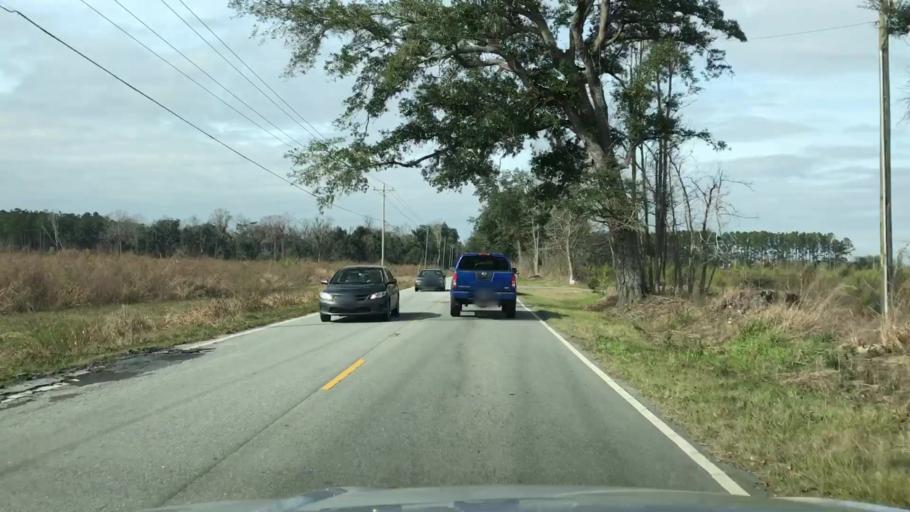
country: US
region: South Carolina
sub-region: Charleston County
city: Shell Point
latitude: 32.7725
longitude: -80.0820
